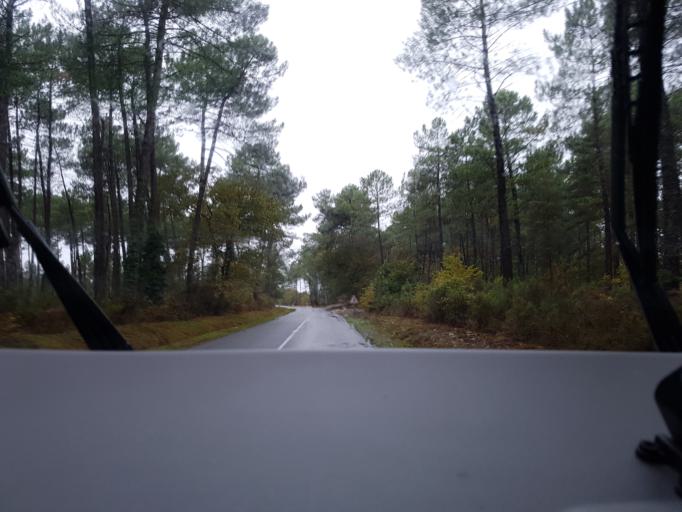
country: FR
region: Aquitaine
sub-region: Departement de la Gironde
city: Belin-Beliet
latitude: 44.4964
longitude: -0.6590
